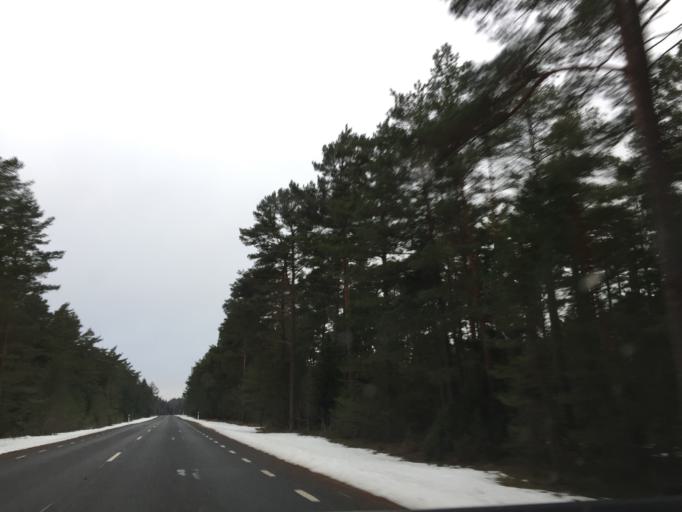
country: EE
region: Saare
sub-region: Kuressaare linn
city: Kuressaare
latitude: 58.5495
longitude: 22.3313
